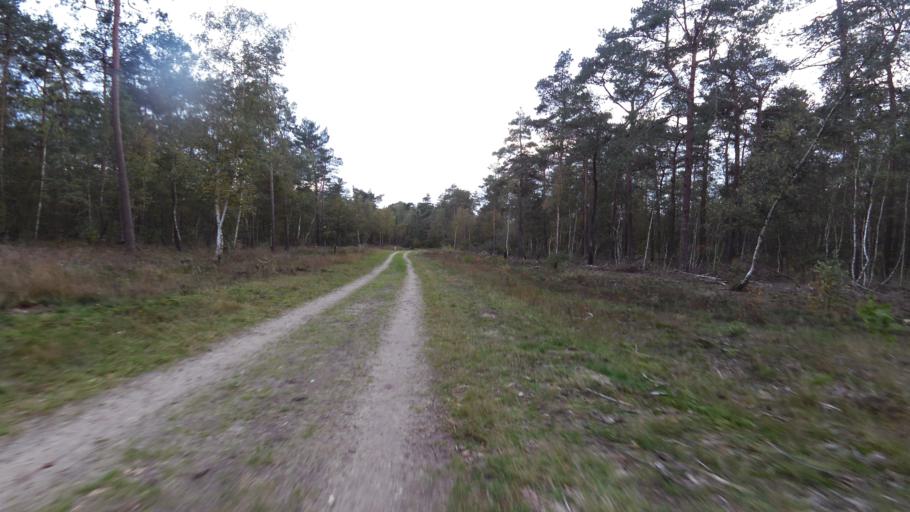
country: NL
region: Gelderland
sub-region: Gemeente Elburg
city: Elburg
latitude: 52.3972
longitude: 5.8563
